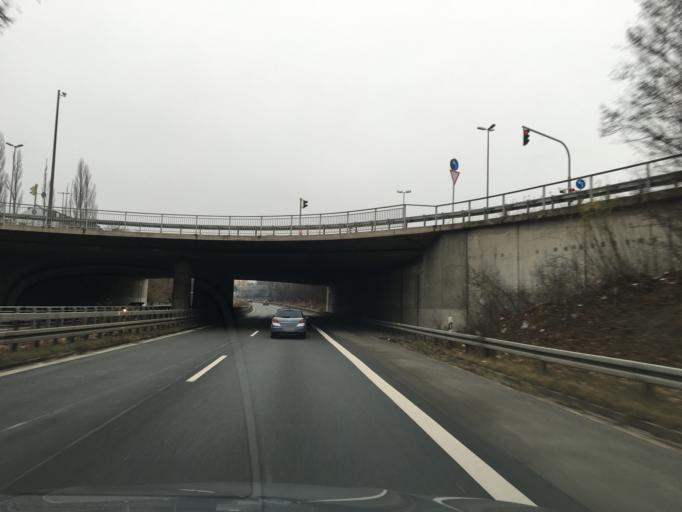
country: DE
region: Bavaria
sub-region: Regierungsbezirk Mittelfranken
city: Nuernberg
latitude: 49.4290
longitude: 11.0630
